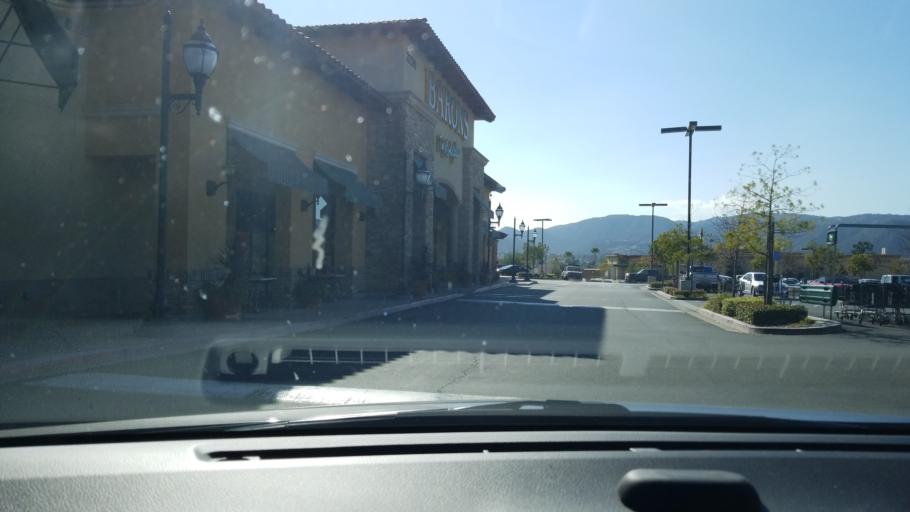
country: US
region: California
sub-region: Riverside County
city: Wildomar
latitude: 33.5911
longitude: -117.2498
